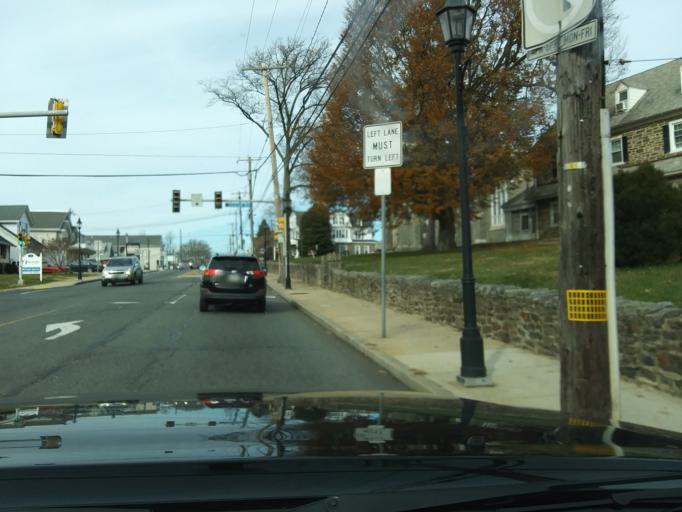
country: US
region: Pennsylvania
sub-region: Montgomery County
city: Rockledge
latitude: 40.0798
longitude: -75.0881
